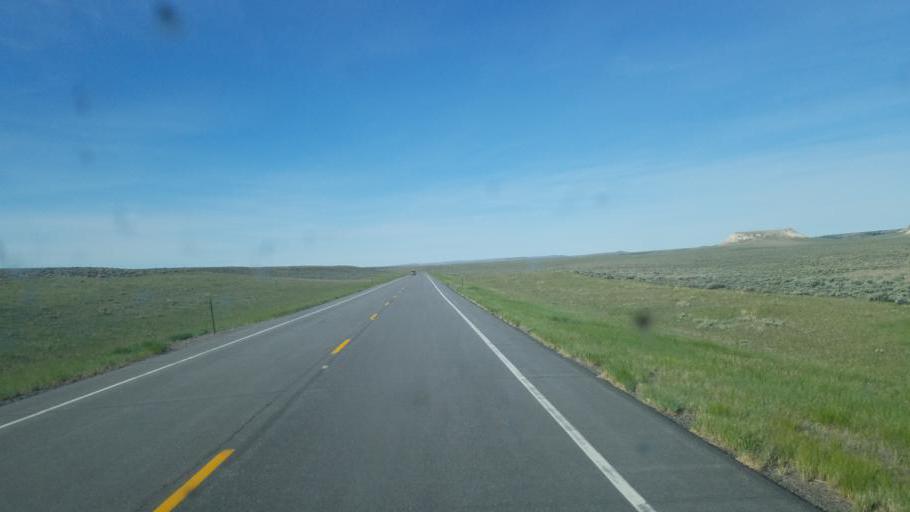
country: US
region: Wyoming
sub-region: Fremont County
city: Riverton
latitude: 42.6556
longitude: -108.1884
